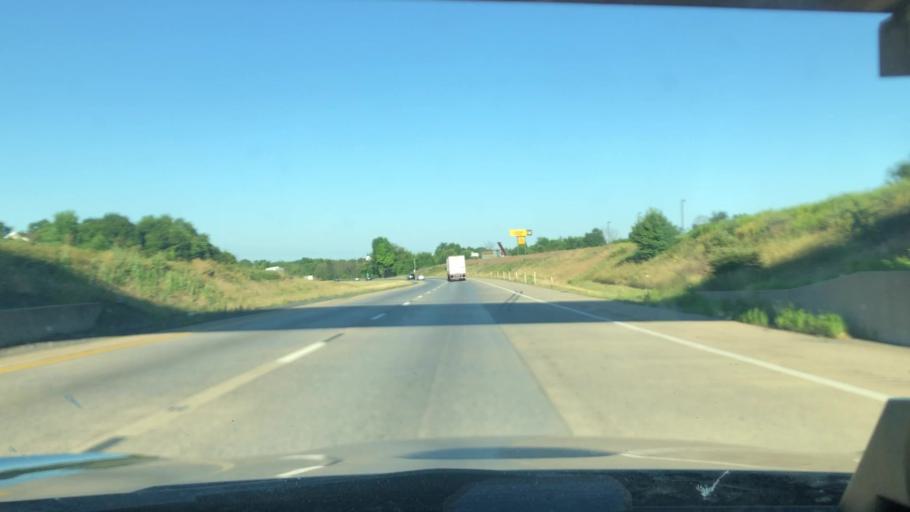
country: US
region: Pennsylvania
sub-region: Dauphin County
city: Skyline View
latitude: 40.3506
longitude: -76.7304
